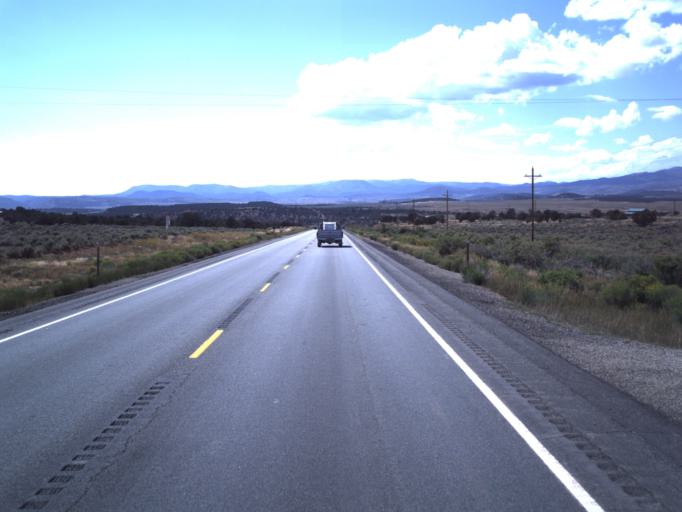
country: US
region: Utah
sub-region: Duchesne County
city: Duchesne
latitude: 40.2082
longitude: -110.7413
